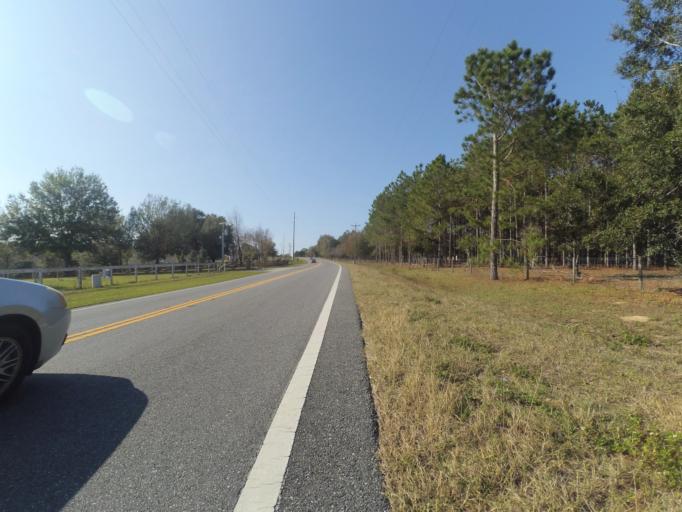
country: US
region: Florida
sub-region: Lake County
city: Umatilla
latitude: 28.9676
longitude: -81.6628
